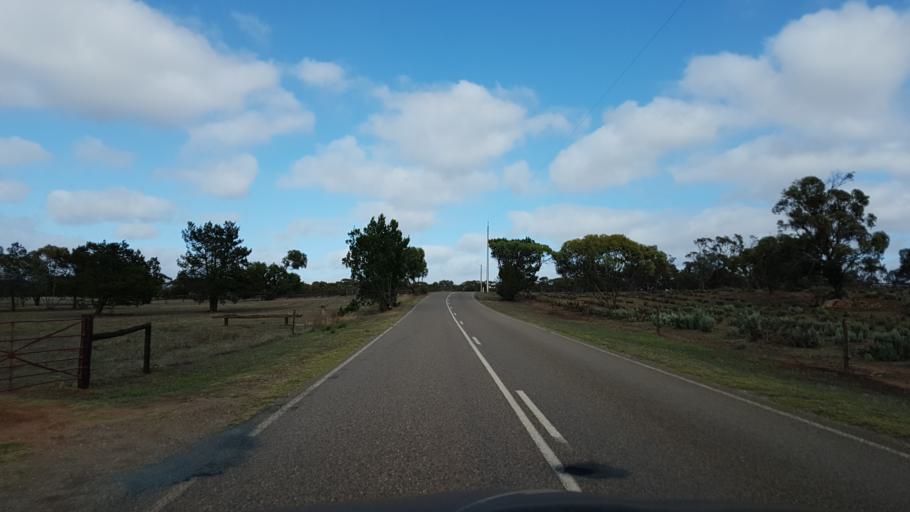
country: AU
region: South Australia
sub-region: Murray Bridge
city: Murray Bridge
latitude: -35.1145
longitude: 139.2175
